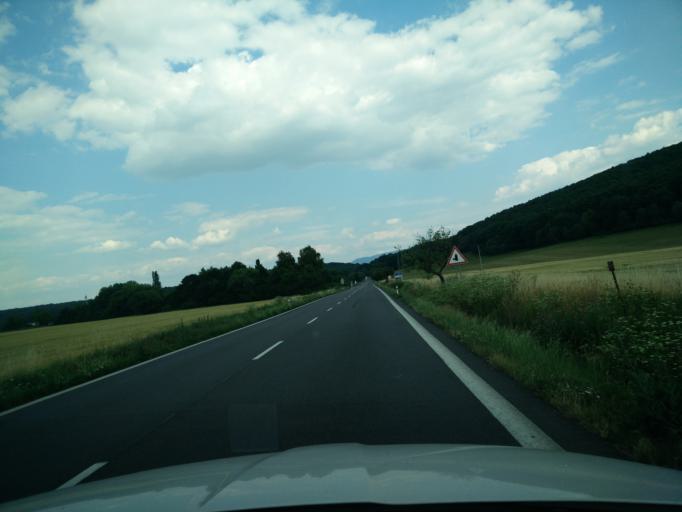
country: SK
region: Nitriansky
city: Novaky
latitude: 48.7222
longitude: 18.4915
